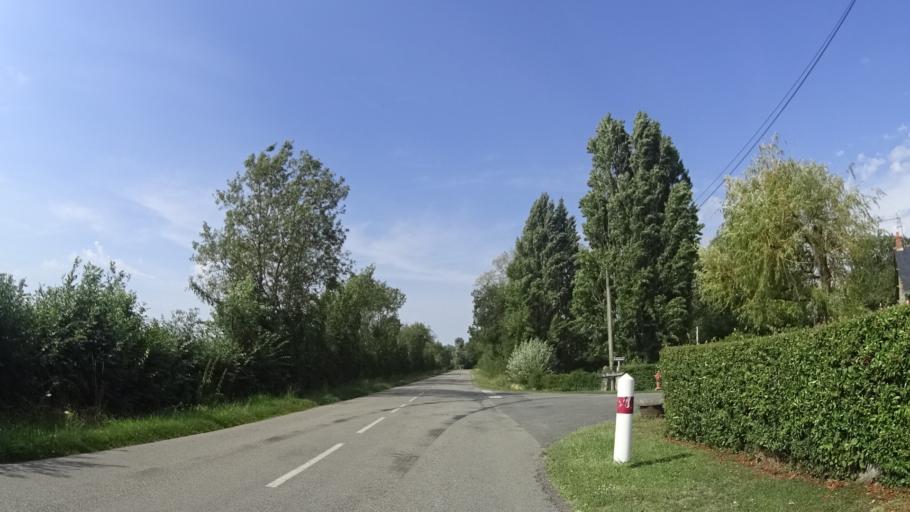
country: FR
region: Pays de la Loire
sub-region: Departement de la Loire-Atlantique
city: Saffre
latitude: 47.4917
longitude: -1.5984
